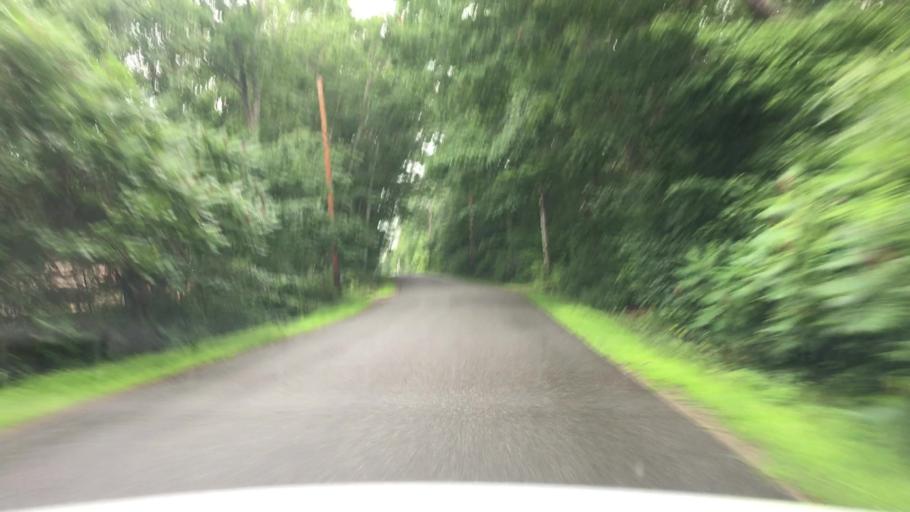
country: US
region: Maine
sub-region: Knox County
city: Hope
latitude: 44.2171
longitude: -69.1811
